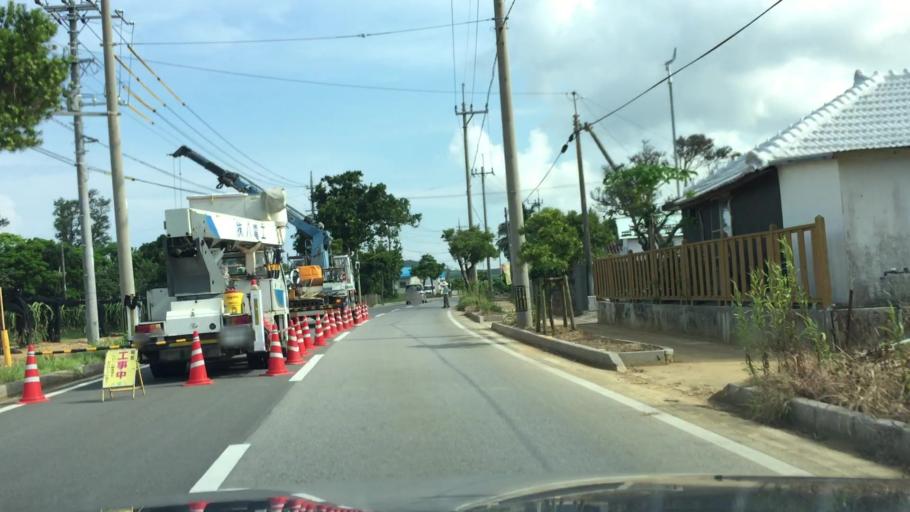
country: JP
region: Okinawa
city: Ishigaki
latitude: 24.4636
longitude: 124.2504
